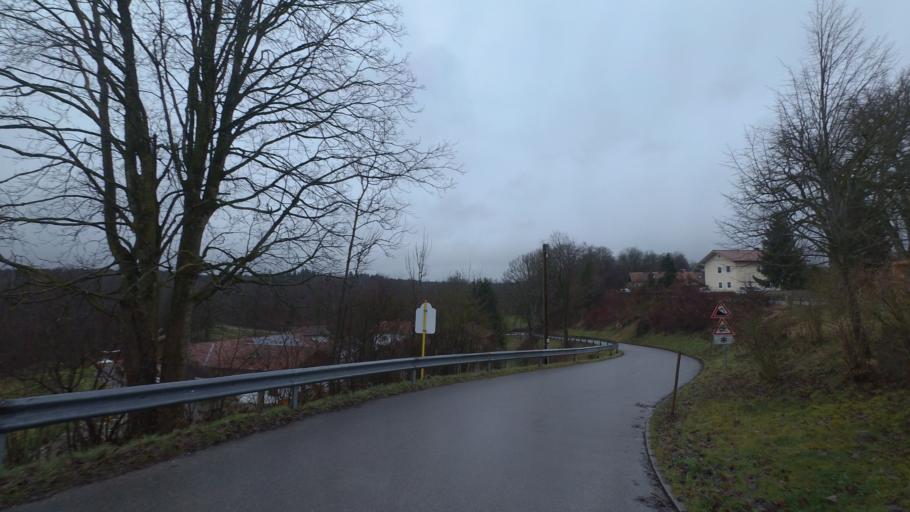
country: DE
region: Bavaria
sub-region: Upper Bavaria
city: Nussdorf
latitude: 47.9085
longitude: 12.6185
